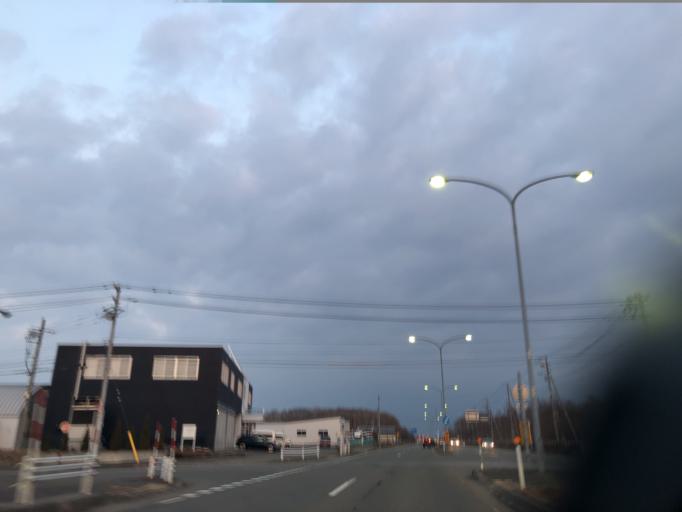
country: JP
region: Hokkaido
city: Chitose
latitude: 42.8210
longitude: 141.6738
